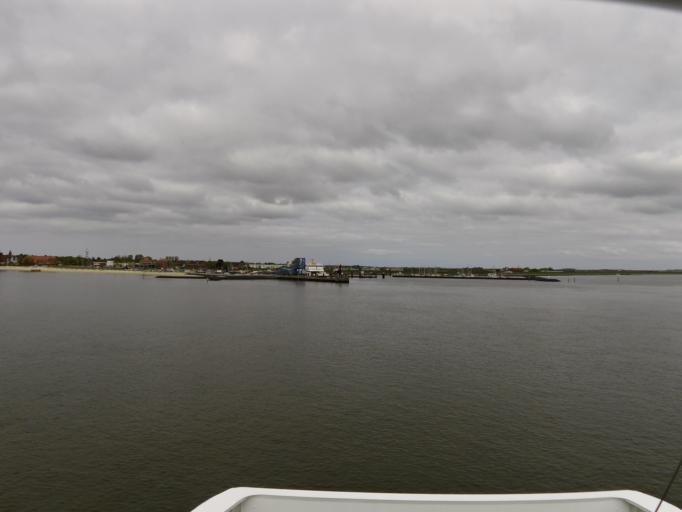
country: DE
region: Schleswig-Holstein
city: Wyk auf Fohr
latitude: 54.6908
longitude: 8.5824
